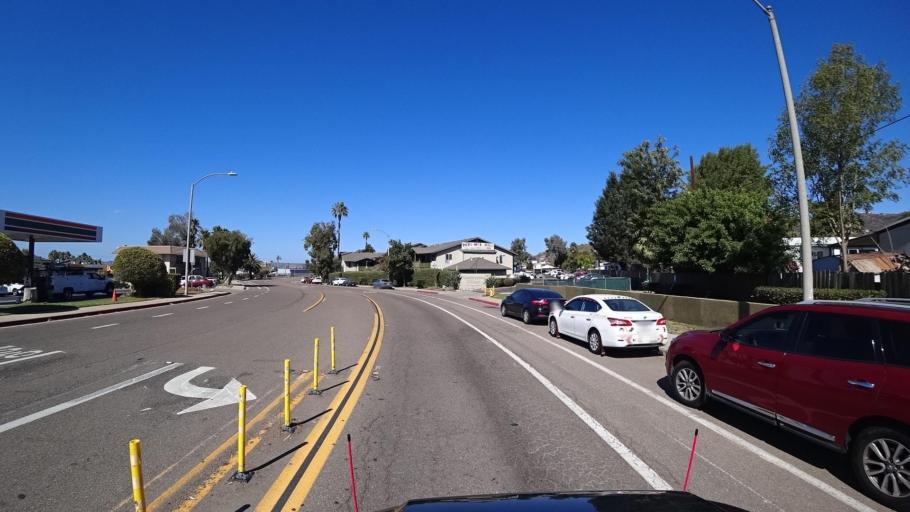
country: US
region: California
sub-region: San Diego County
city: Santee
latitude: 32.8195
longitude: -116.9590
